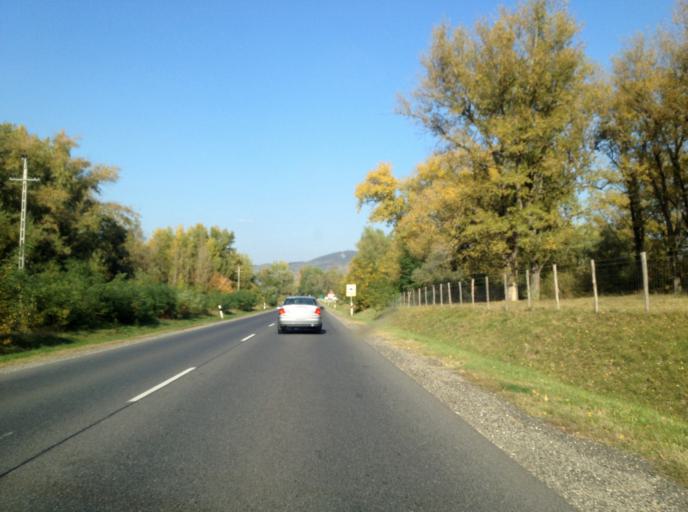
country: HU
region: Komarom-Esztergom
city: Esztergom
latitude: 47.7579
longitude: 18.7430
